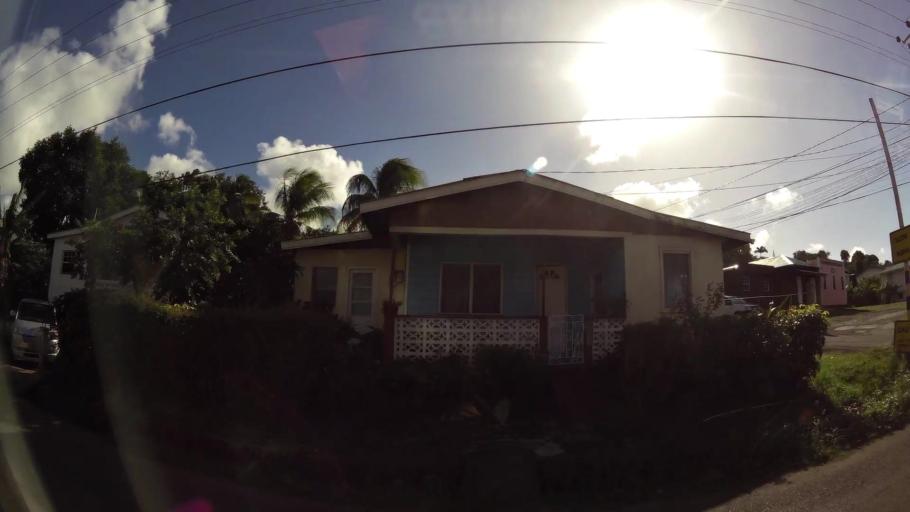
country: LC
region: Castries Quarter
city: Bisee
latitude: 14.0453
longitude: -60.9644
